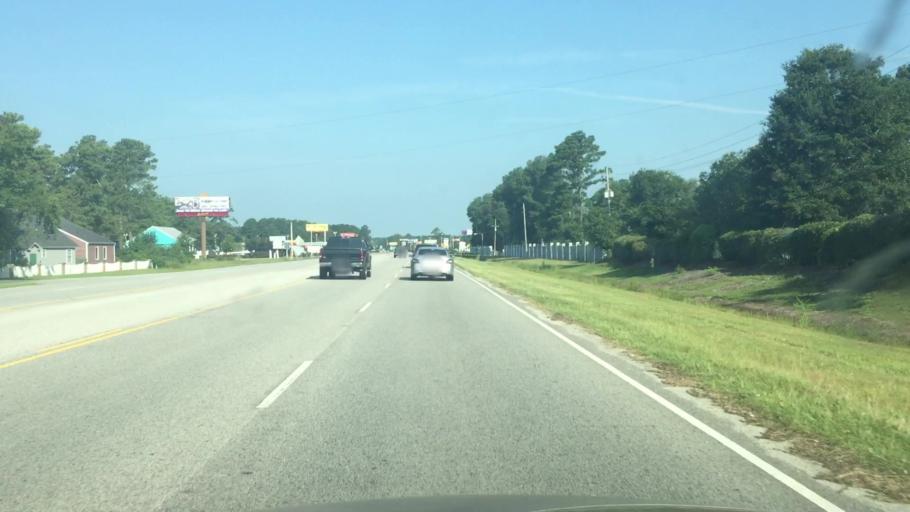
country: US
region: South Carolina
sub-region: Horry County
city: Little River
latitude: 33.8688
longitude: -78.6671
